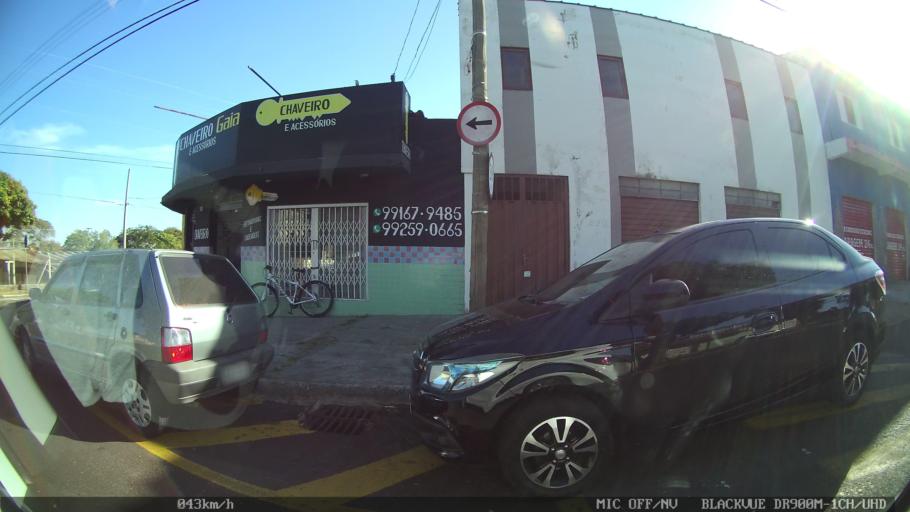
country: BR
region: Sao Paulo
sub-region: Franca
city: Franca
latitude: -20.5079
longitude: -47.4156
